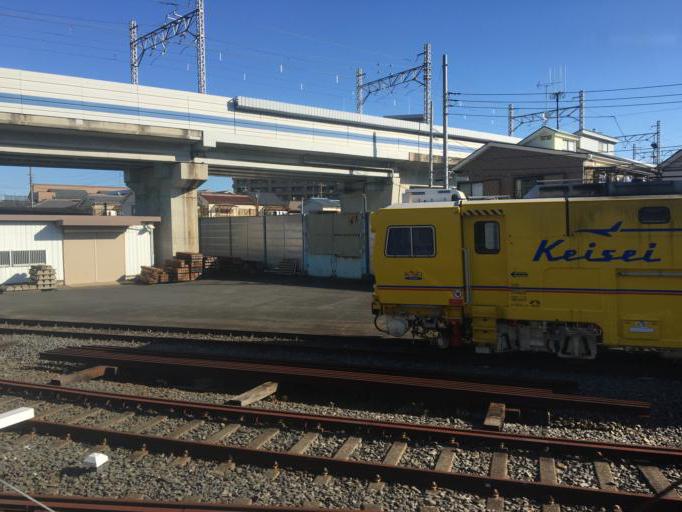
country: JP
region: Chiba
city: Matsudo
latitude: 35.7488
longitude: 139.8741
